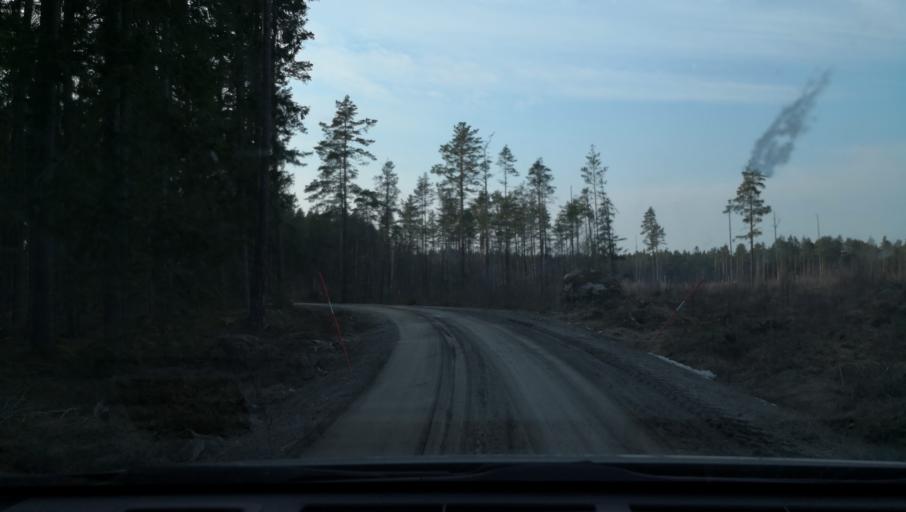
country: SE
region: OErebro
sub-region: Lindesbergs Kommun
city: Frovi
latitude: 59.3570
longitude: 15.3340
